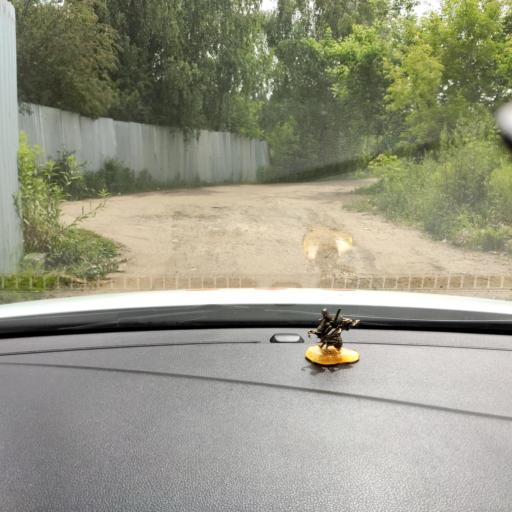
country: RU
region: Tatarstan
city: Staroye Arakchino
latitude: 55.8895
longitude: 49.0437
